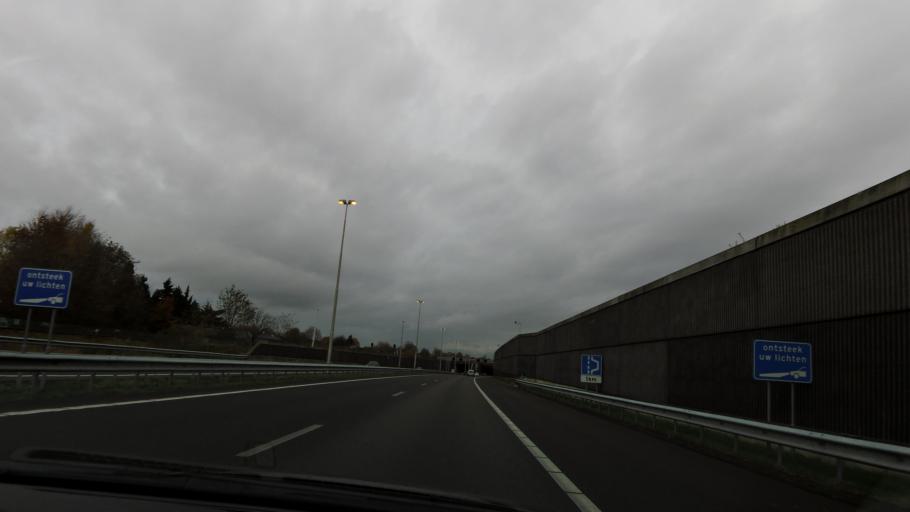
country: NL
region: Limburg
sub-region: Gemeente Roermond
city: Leeuwen
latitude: 51.2316
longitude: 6.0271
